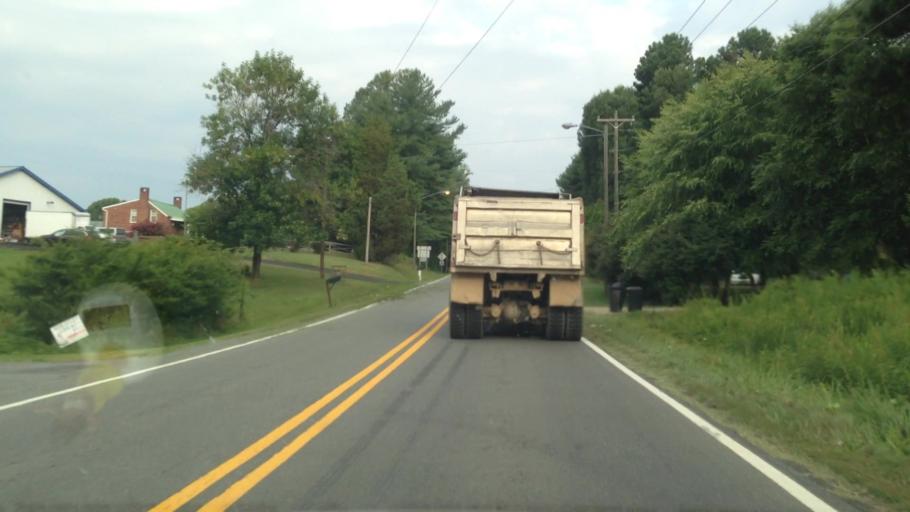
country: US
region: North Carolina
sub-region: Forsyth County
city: Walkertown
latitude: 36.1845
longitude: -80.2024
